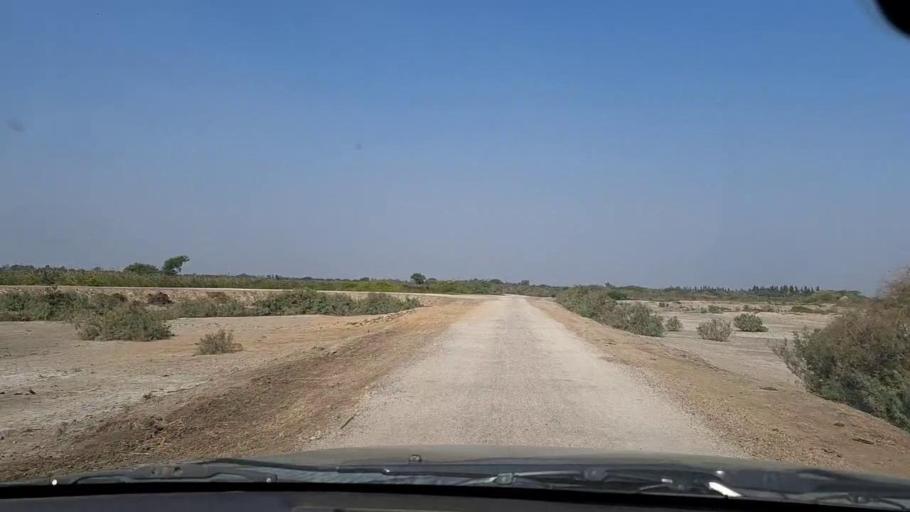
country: PK
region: Sindh
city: Chuhar Jamali
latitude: 24.4351
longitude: 67.7994
